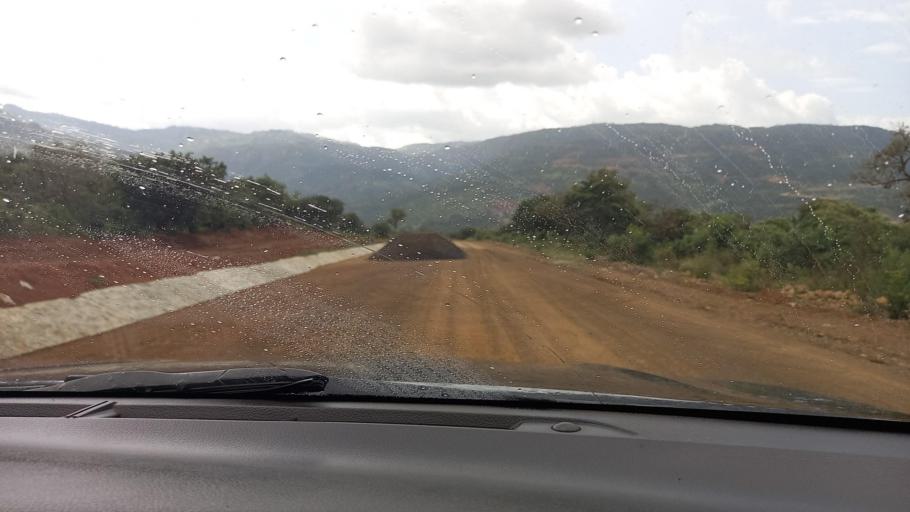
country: ET
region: Southern Nations, Nationalities, and People's Region
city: Mizan Teferi
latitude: 6.1869
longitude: 35.6897
